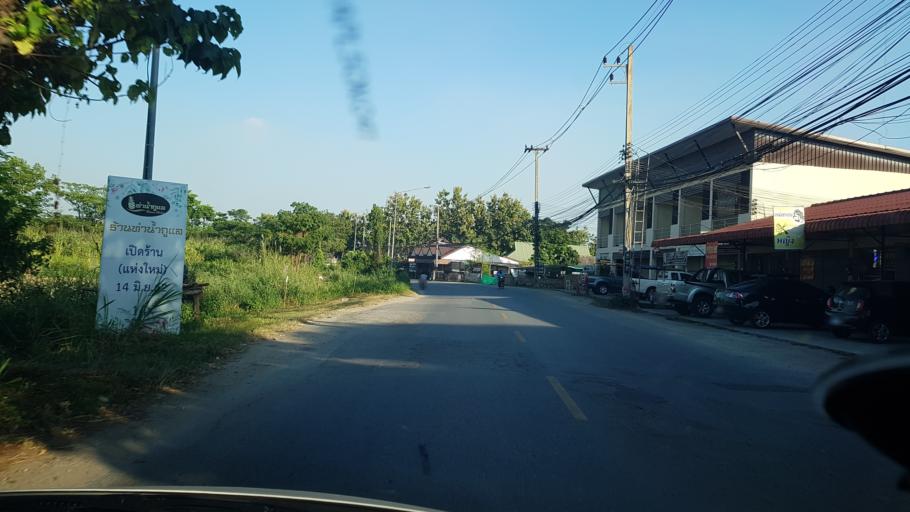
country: TH
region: Chiang Rai
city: Chiang Rai
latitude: 19.9292
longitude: 99.8282
